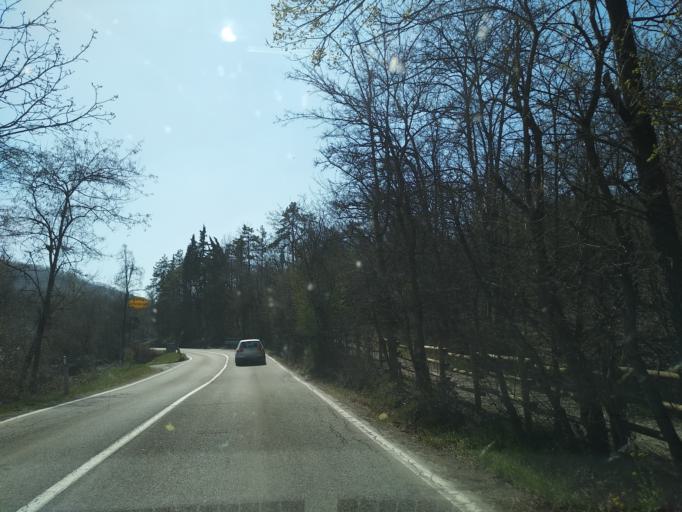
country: IT
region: Emilia-Romagna
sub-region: Provincia di Reggio Emilia
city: Vezzano sul Crostolo
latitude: 44.5886
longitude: 10.5356
